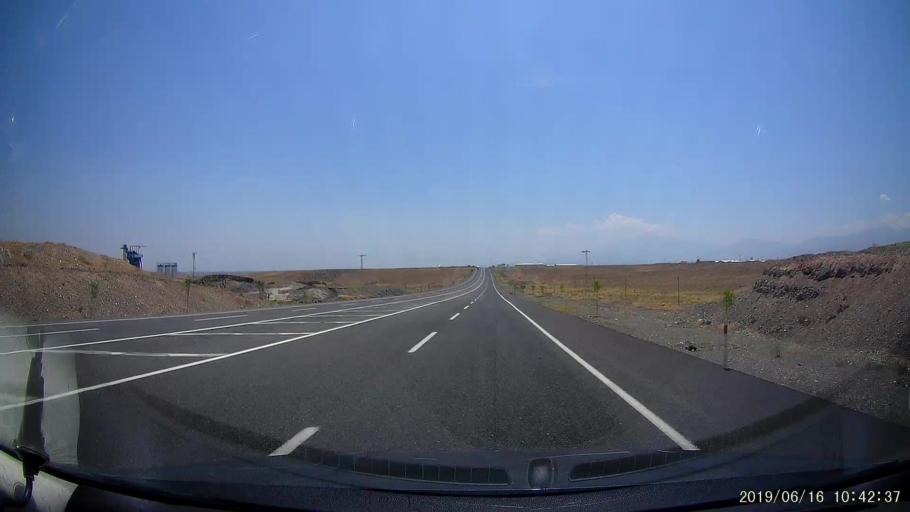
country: AM
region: Armavir
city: Shenavan
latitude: 40.0408
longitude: 43.8103
